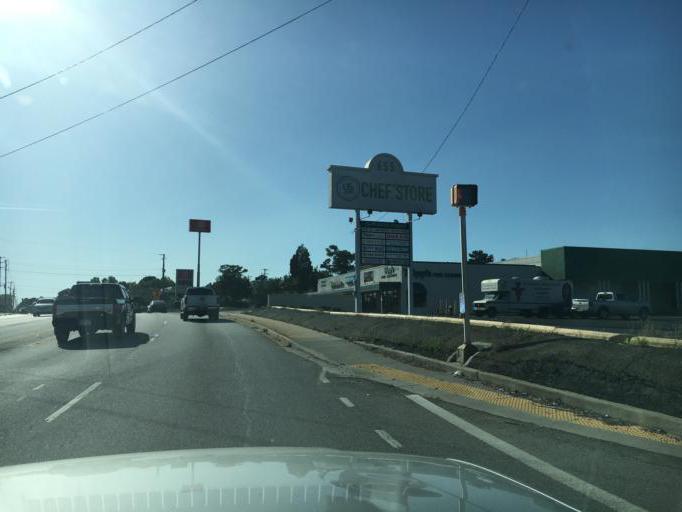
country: US
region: South Carolina
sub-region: Lexington County
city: Saint Andrews
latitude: 34.0449
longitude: -81.1224
